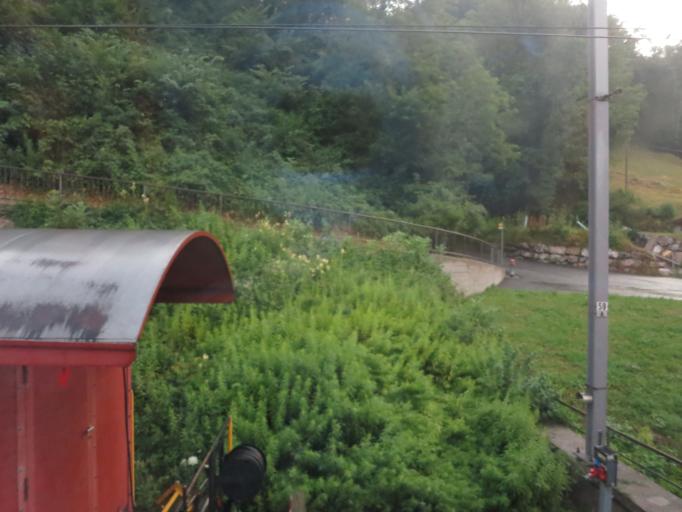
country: CH
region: Glarus
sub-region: Glarus
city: Niederurnen
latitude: 47.1343
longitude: 9.0636
